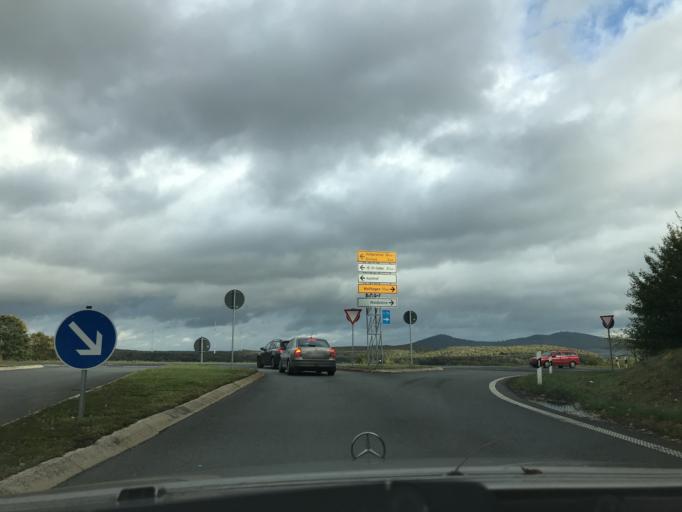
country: DE
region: Hesse
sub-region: Regierungsbezirk Kassel
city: Breuna
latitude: 51.4007
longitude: 9.1839
